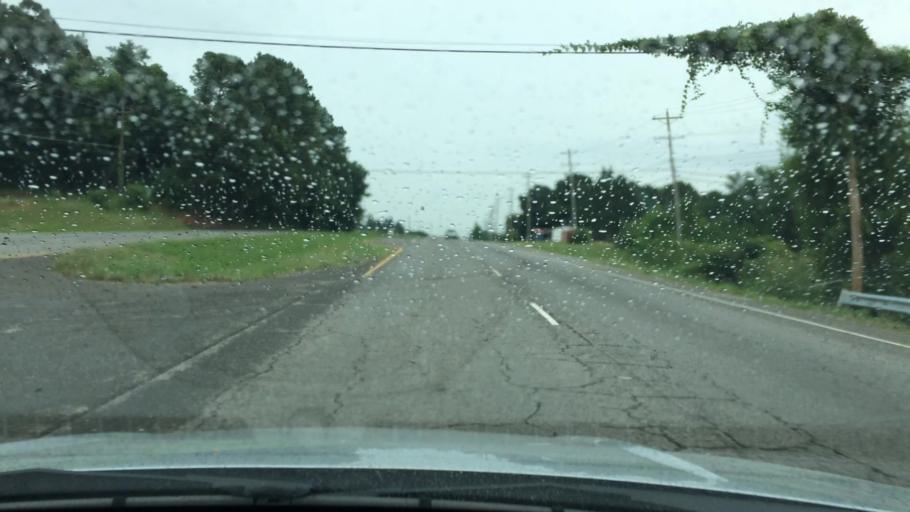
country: US
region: Tennessee
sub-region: Jefferson County
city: Jefferson City
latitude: 36.1706
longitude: -83.4057
